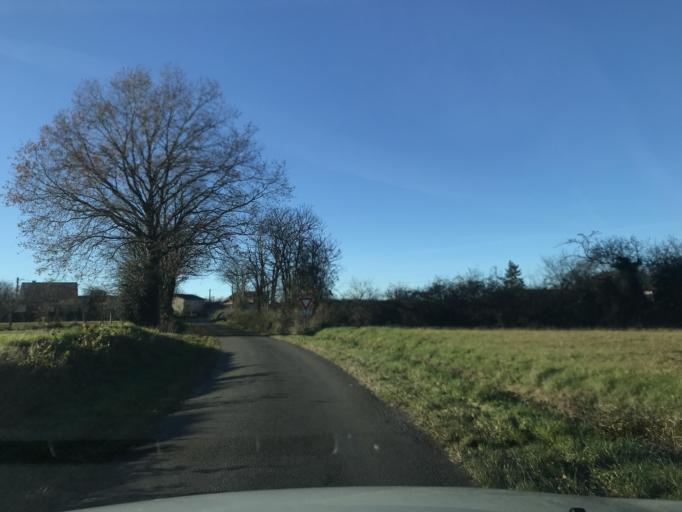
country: FR
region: Poitou-Charentes
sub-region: Departement de la Charente
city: Saint-Claud
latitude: 45.8481
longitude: 0.5026
